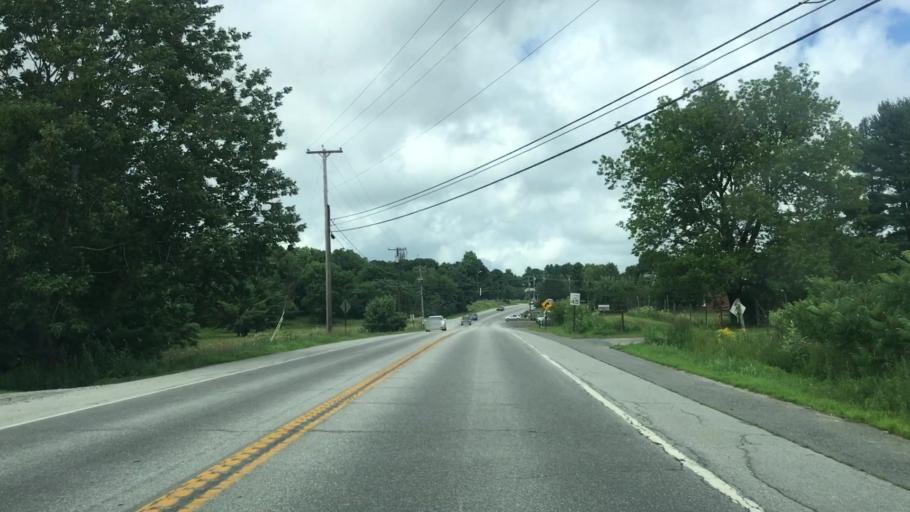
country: US
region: Maine
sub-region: Kennebec County
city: Hallowell
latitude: 44.2834
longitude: -69.7769
